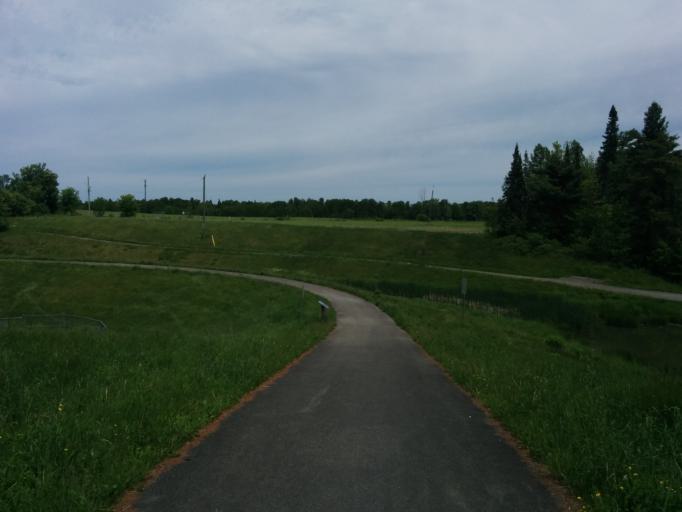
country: CA
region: Ontario
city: Clarence-Rockland
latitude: 45.4845
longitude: -75.4673
